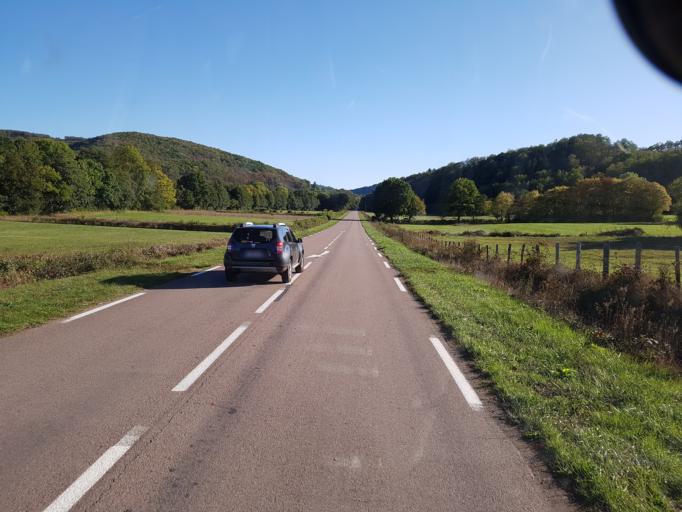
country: FR
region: Bourgogne
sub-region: Departement de la Cote-d'Or
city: Saulieu
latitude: 47.1107
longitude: 4.2281
